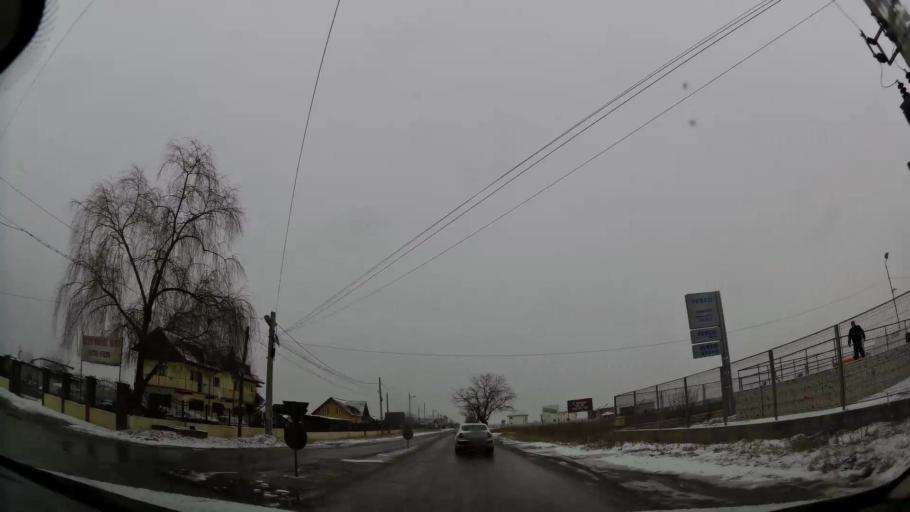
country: RO
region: Dambovita
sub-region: Comuna Ulmi
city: Ulmi
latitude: 44.8952
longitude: 25.5104
